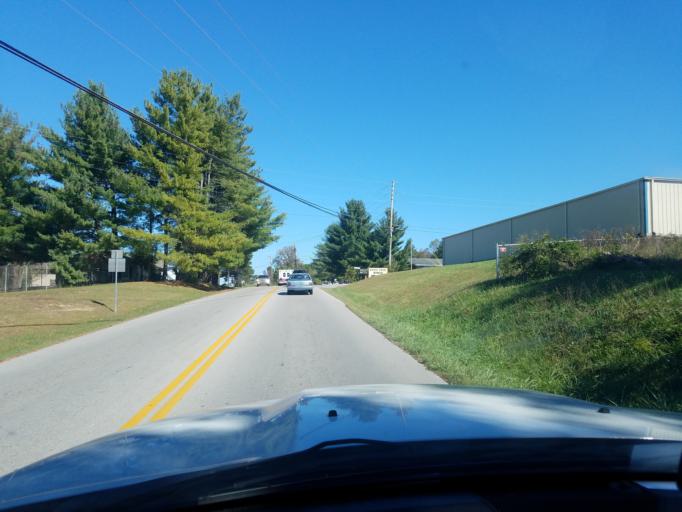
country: US
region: Kentucky
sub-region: Laurel County
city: North Corbin
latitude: 36.9732
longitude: -84.0915
